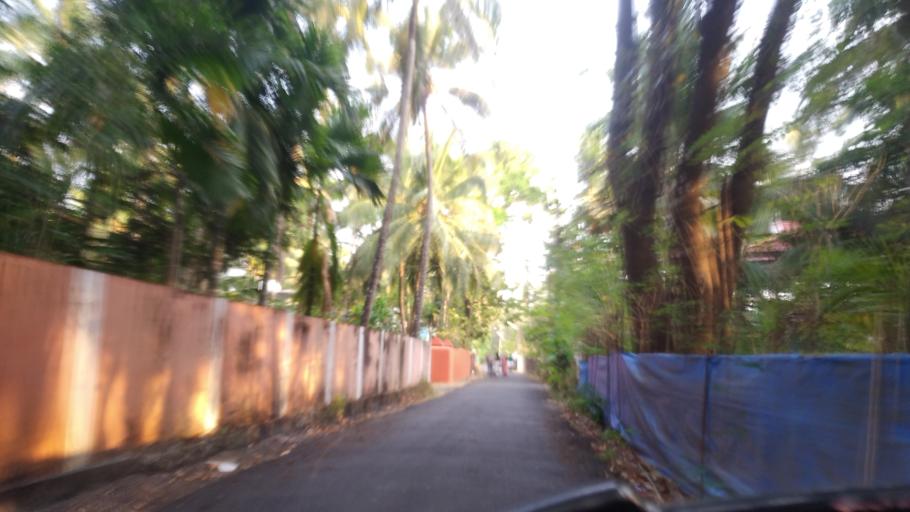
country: IN
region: Kerala
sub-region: Thrissur District
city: Thanniyam
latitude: 10.4178
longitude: 76.0860
